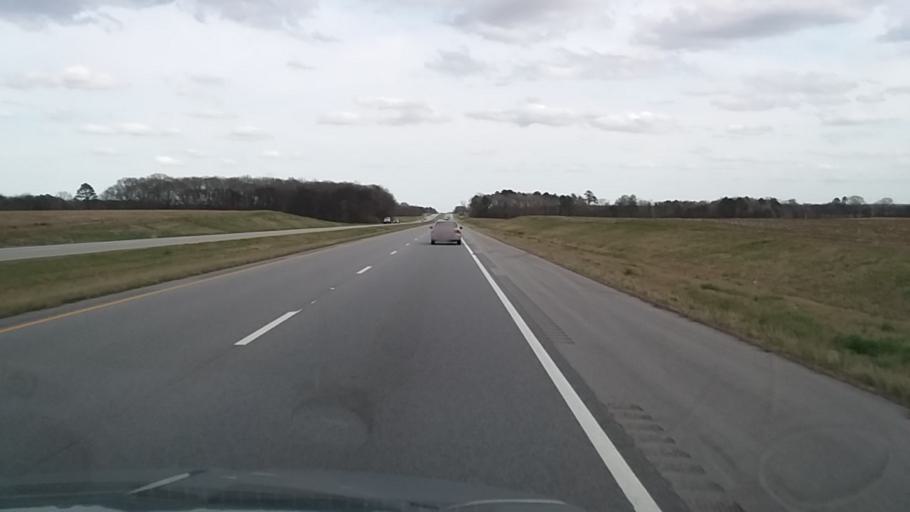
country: US
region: Alabama
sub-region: Lawrence County
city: Town Creek
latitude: 34.6830
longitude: -87.4898
